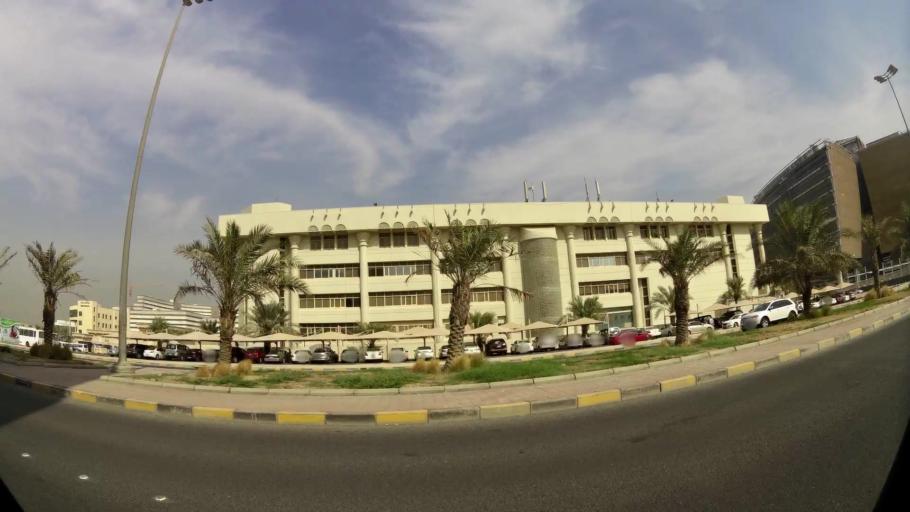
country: KW
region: Al Farwaniyah
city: Janub as Surrah
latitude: 29.2713
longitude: 48.0182
